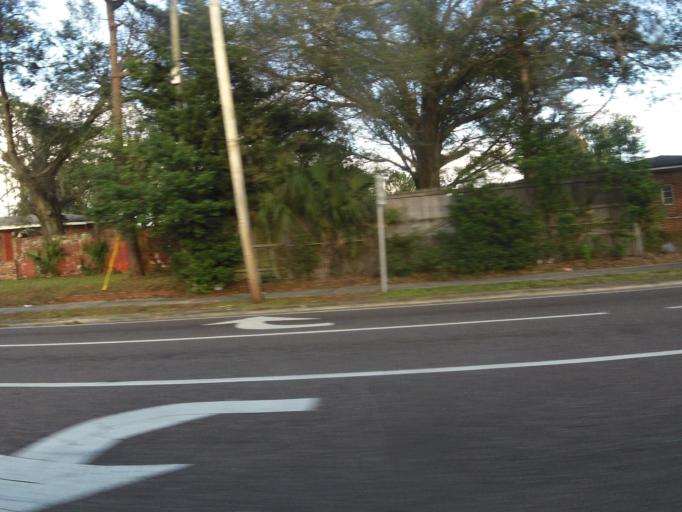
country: US
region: Florida
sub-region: Duval County
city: Jacksonville
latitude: 30.3514
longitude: -81.5896
